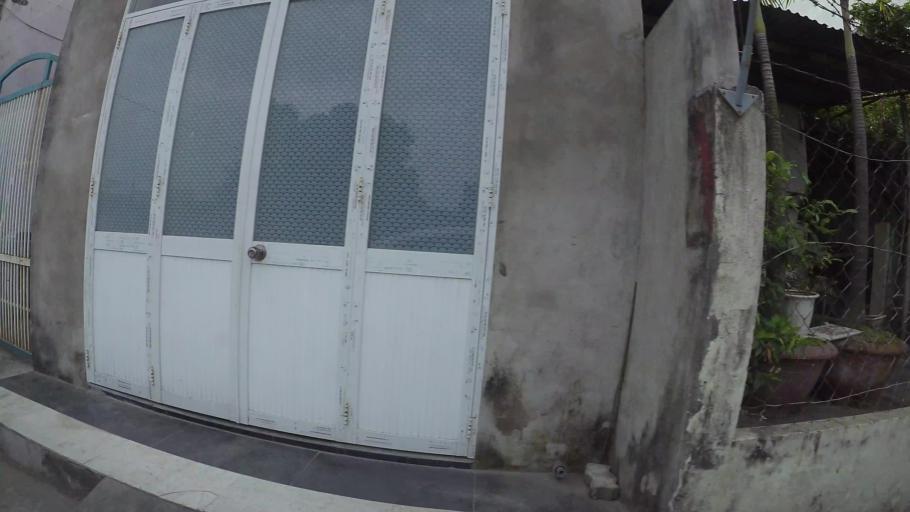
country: VN
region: Da Nang
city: Son Tra
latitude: 16.0827
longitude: 108.2405
